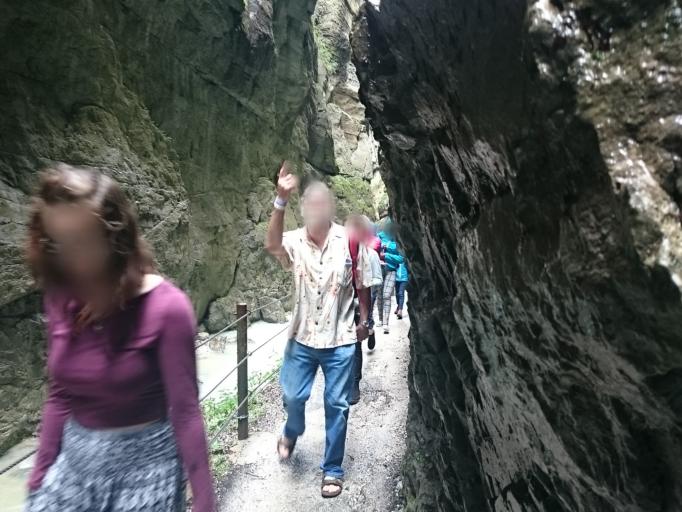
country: DE
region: Bavaria
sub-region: Upper Bavaria
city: Garmisch-Partenkirchen
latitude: 47.4634
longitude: 11.1238
